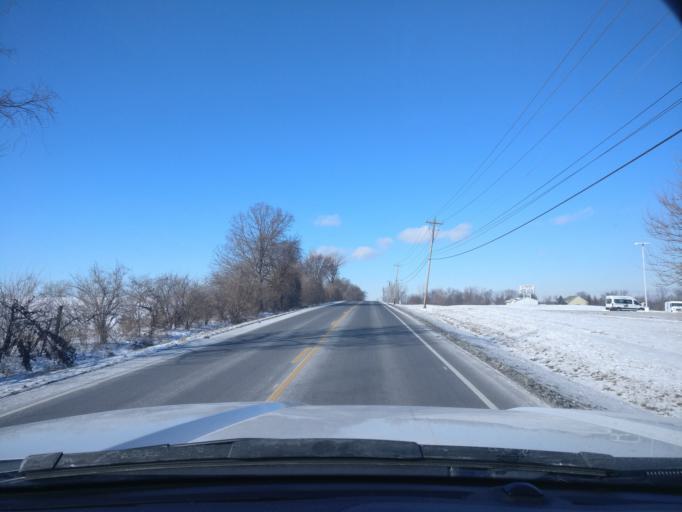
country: US
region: Ohio
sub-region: Warren County
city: Hunter
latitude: 39.5130
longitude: -84.2692
